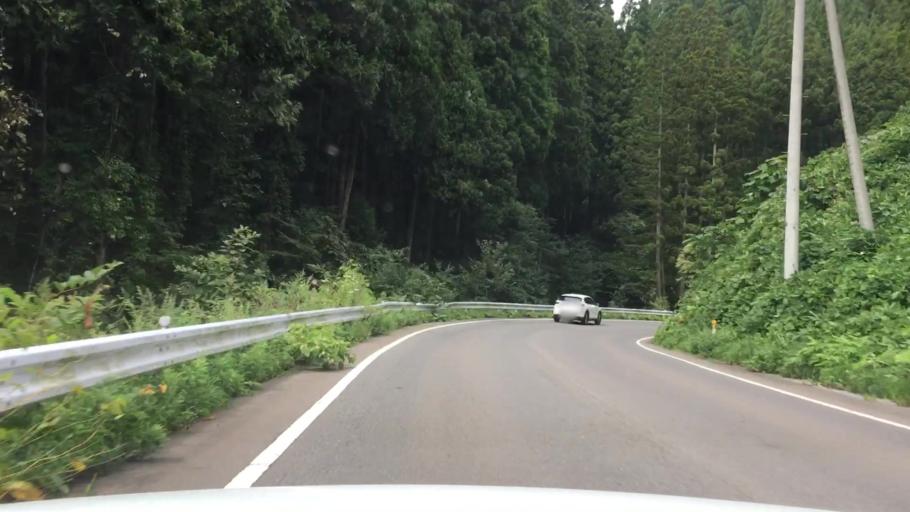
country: JP
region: Aomori
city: Shimokizukuri
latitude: 40.7336
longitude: 140.2504
